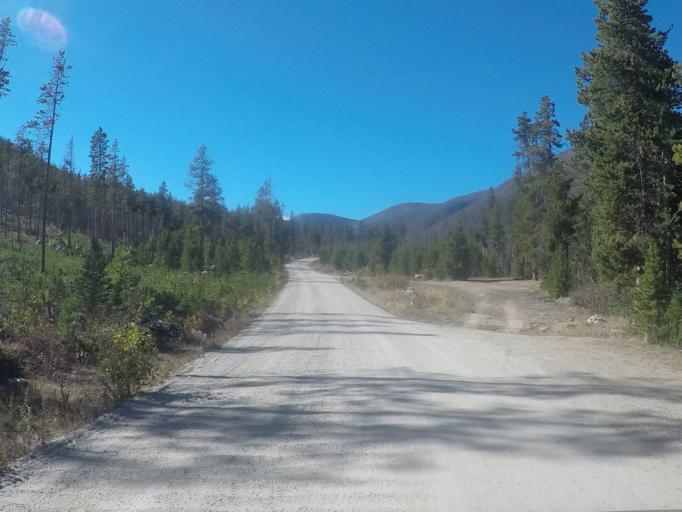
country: US
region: Montana
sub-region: Carbon County
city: Red Lodge
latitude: 45.1709
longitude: -109.4242
